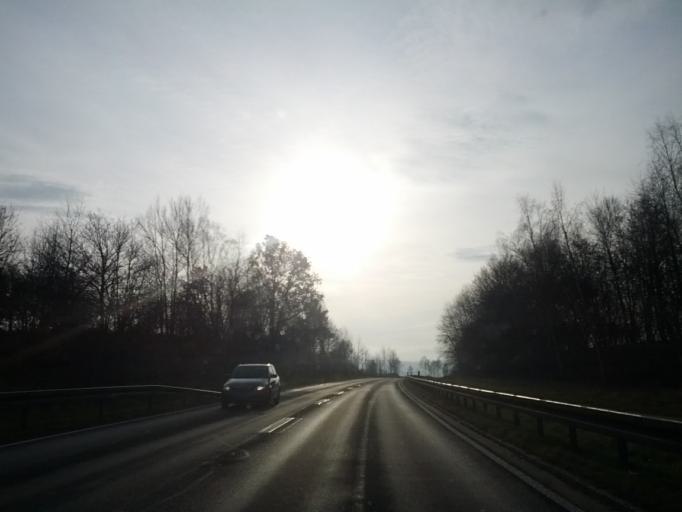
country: DE
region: Thuringia
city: Fambach
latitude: 50.7541
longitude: 10.3560
